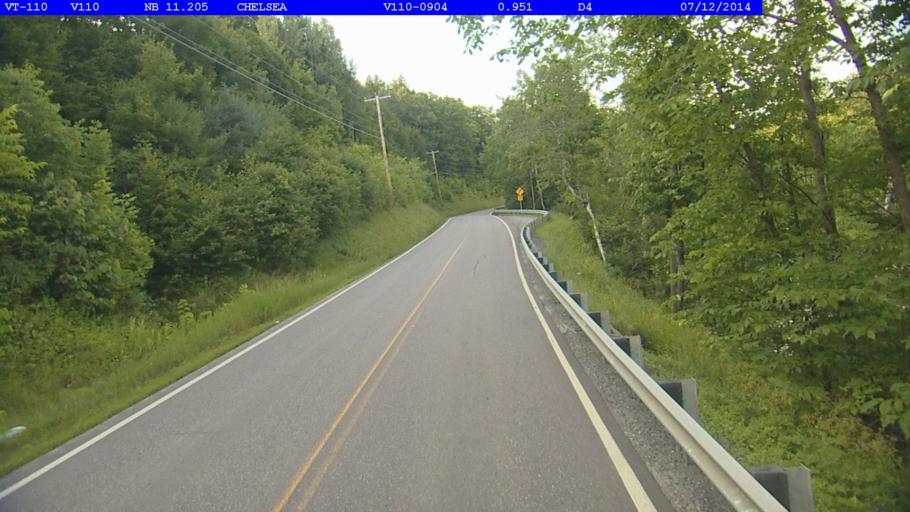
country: US
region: Vermont
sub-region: Orange County
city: Chelsea
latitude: 43.9644
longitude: -72.4633
